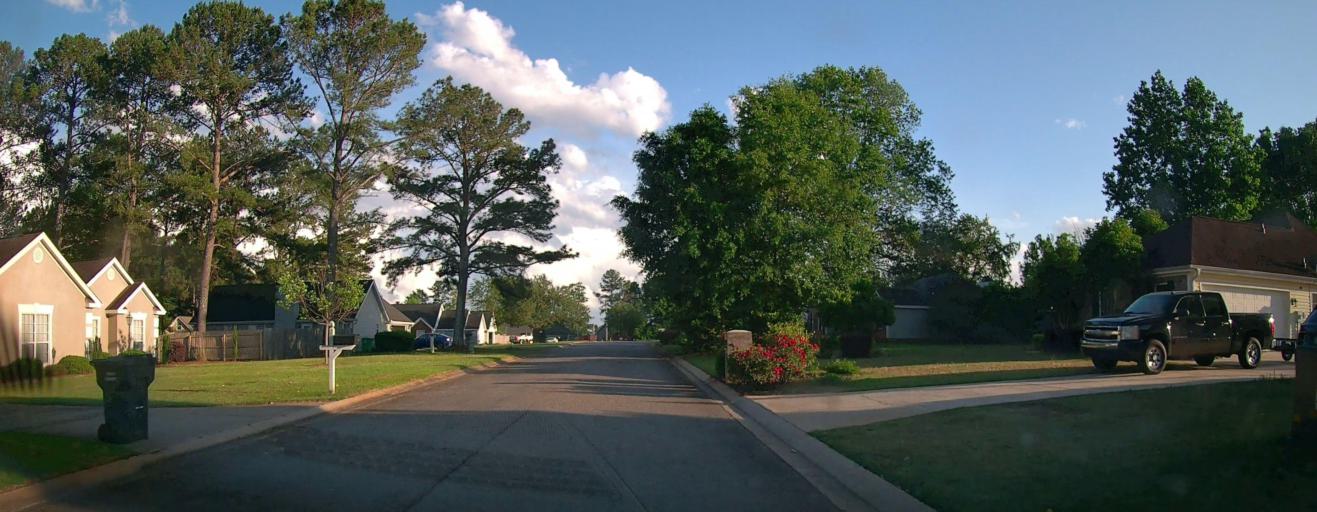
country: US
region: Georgia
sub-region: Houston County
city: Centerville
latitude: 32.6370
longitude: -83.7166
